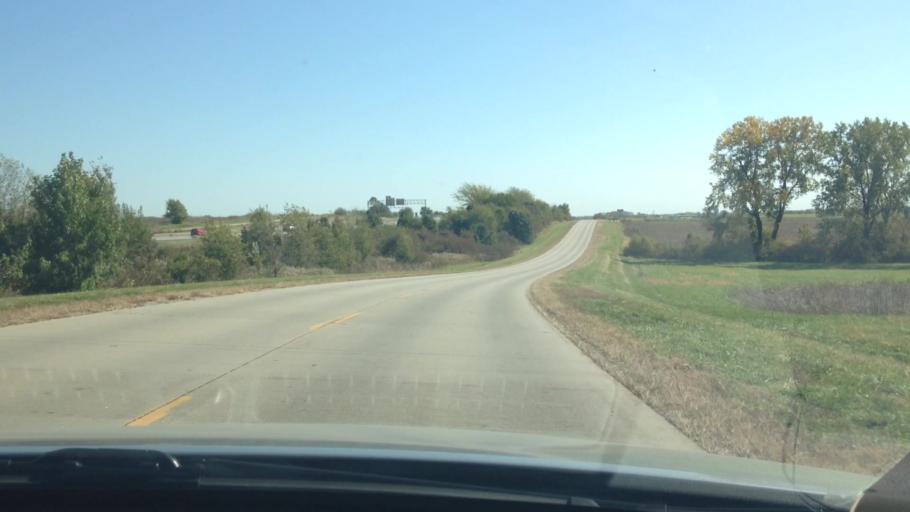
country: US
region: Missouri
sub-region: Platte County
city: Platte City
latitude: 39.3372
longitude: -94.7293
